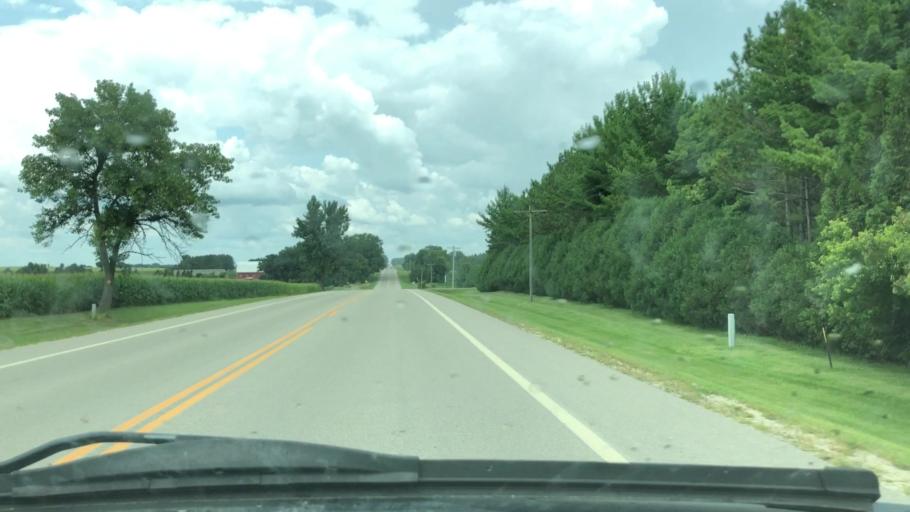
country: US
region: Minnesota
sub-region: Olmsted County
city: Stewartville
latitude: 43.8678
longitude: -92.5286
